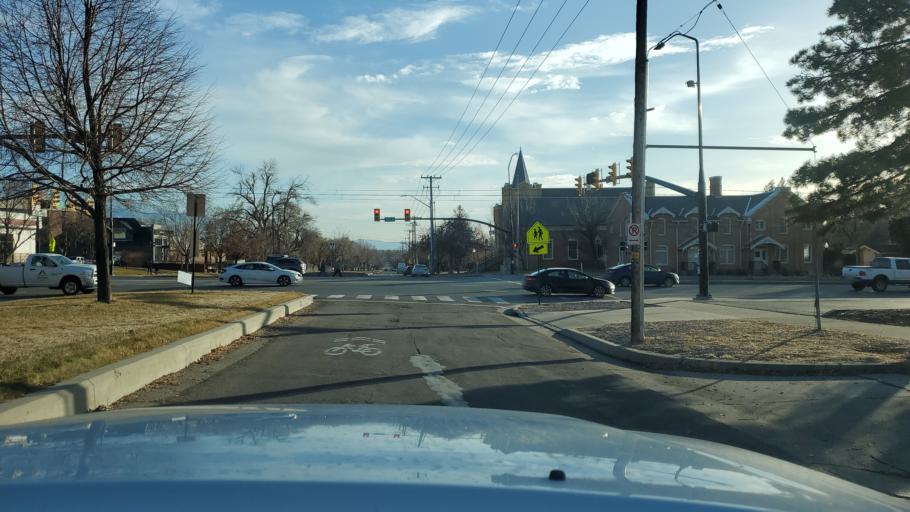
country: US
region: Utah
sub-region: Salt Lake County
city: Salt Lake City
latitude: 40.7611
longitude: -111.8683
